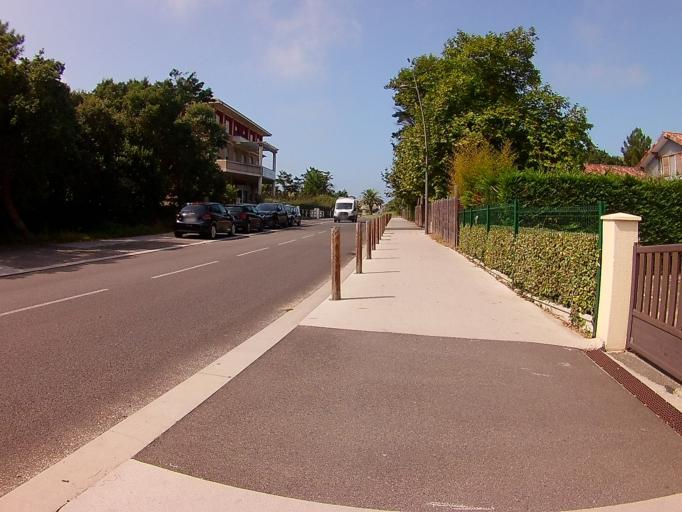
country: FR
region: Aquitaine
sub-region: Departement des Landes
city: Ondres
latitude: 43.5981
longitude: -1.4688
